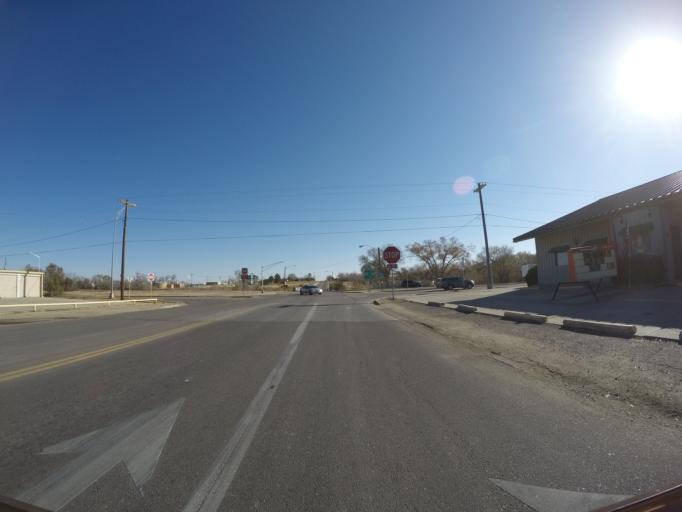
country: US
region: Colorado
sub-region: Otero County
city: La Junta
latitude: 37.9859
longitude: -103.5329
